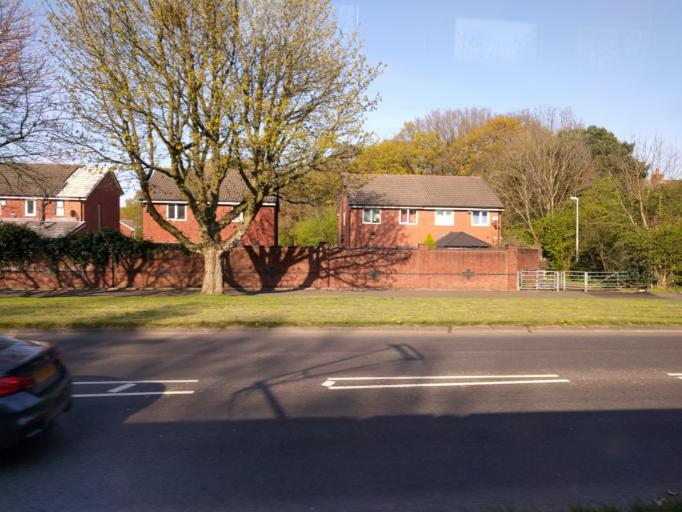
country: GB
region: England
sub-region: Manchester
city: Ringway
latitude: 53.3747
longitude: -2.2522
